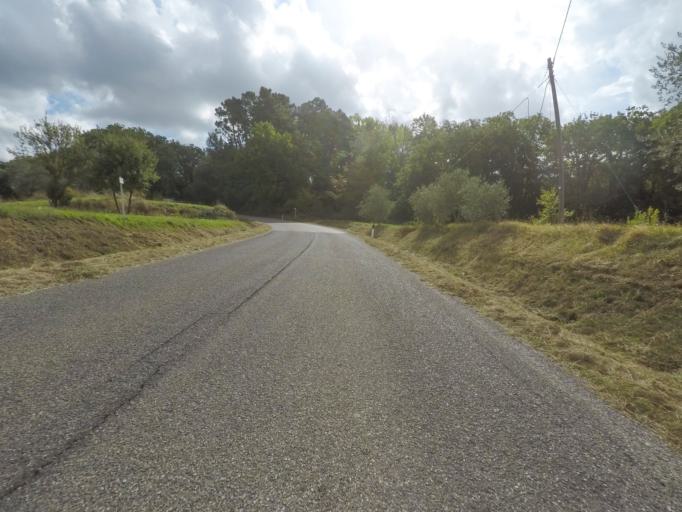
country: IT
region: Tuscany
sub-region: Provincia di Siena
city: Torrita di Siena
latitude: 43.1549
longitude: 11.7766
